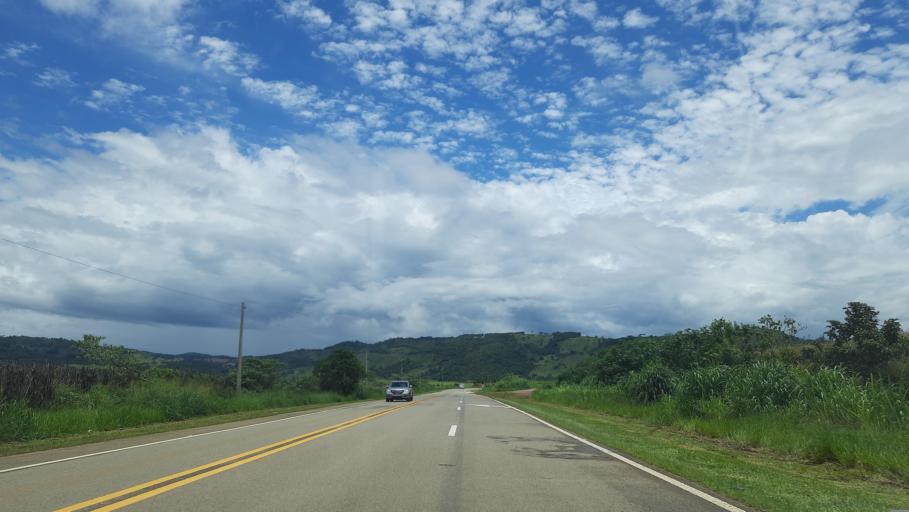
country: BR
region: Sao Paulo
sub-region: Vargem Grande Do Sul
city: Vargem Grande do Sul
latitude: -21.8126
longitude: -46.7875
